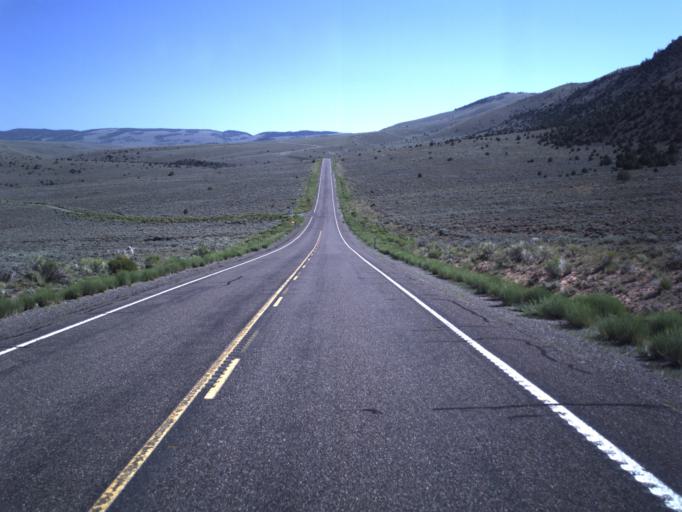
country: US
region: Utah
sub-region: Wayne County
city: Loa
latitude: 38.5170
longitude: -111.5232
